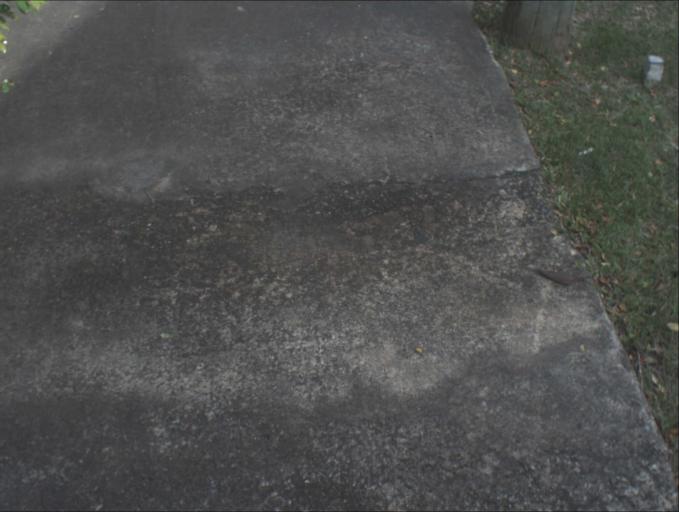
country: AU
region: Queensland
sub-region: Logan
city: Park Ridge South
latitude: -27.6712
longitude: 153.0440
